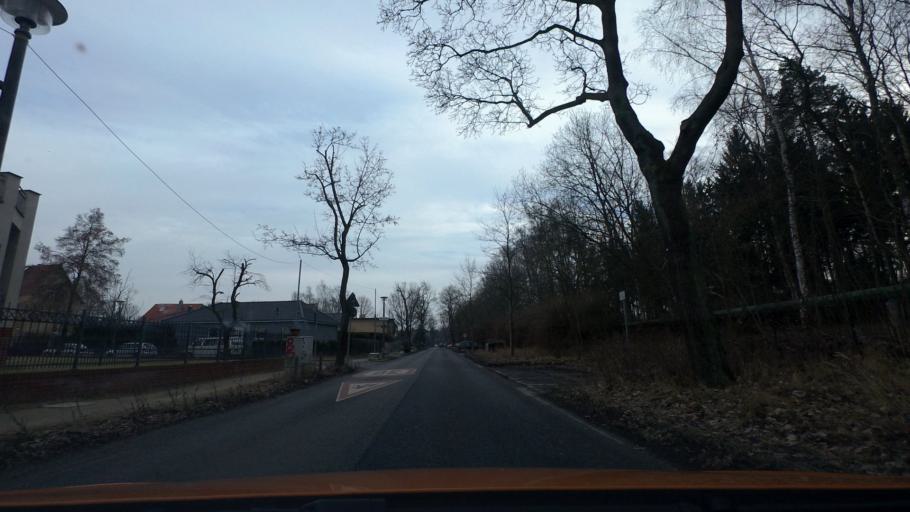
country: DE
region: Berlin
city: Buch
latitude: 52.6439
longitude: 13.4926
